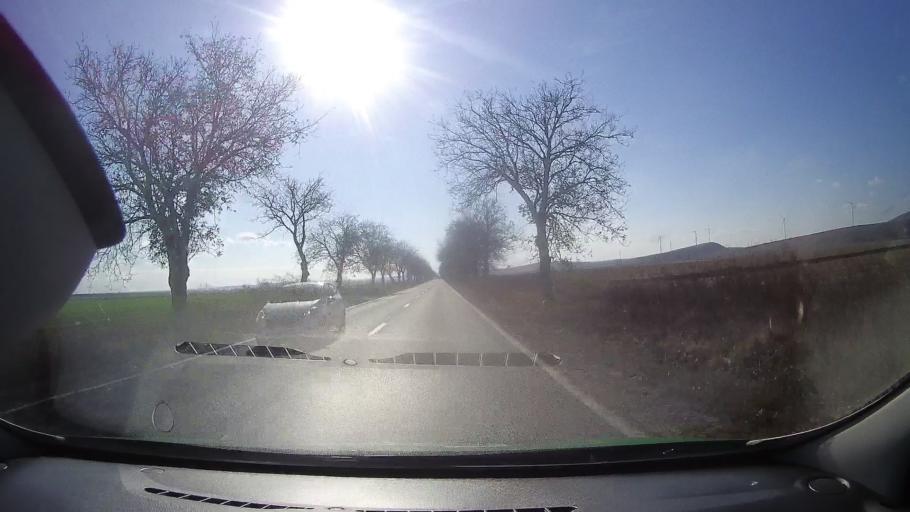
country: RO
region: Tulcea
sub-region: Comuna Ceamurlia de Jos
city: Ceamurlia de Jos
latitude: 44.7925
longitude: 28.6900
